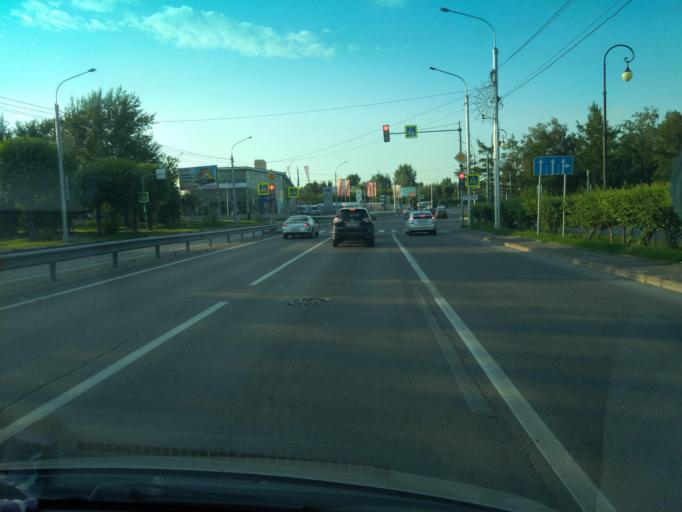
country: RU
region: Krasnoyarskiy
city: Krasnoyarsk
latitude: 56.0231
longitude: 92.8853
